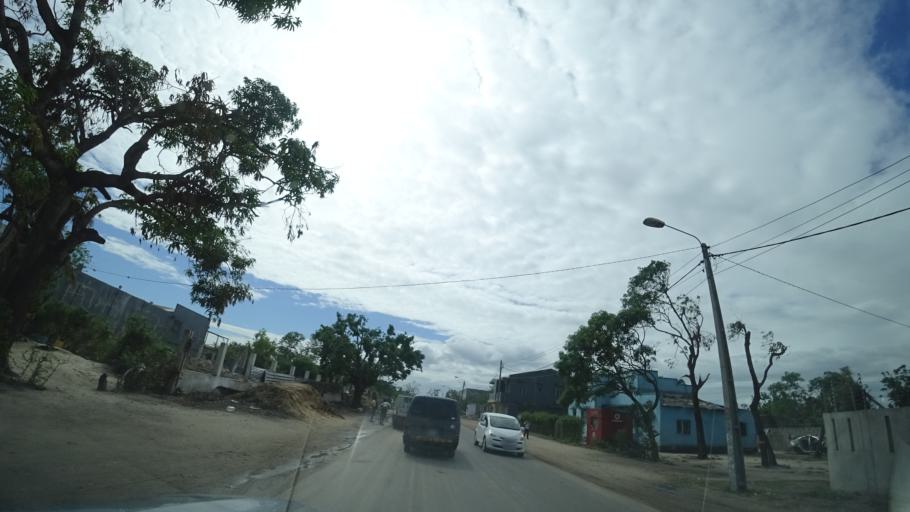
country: MZ
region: Sofala
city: Beira
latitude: -19.7801
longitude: 34.8726
